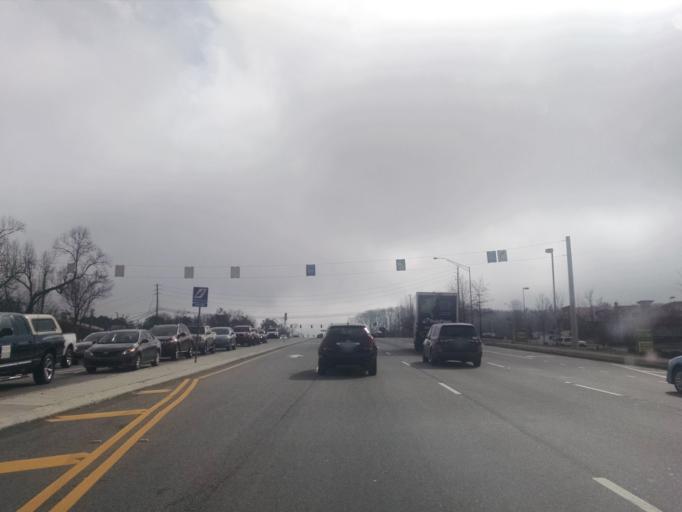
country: US
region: Georgia
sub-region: Gwinnett County
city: Buford
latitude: 34.0891
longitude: -83.9966
